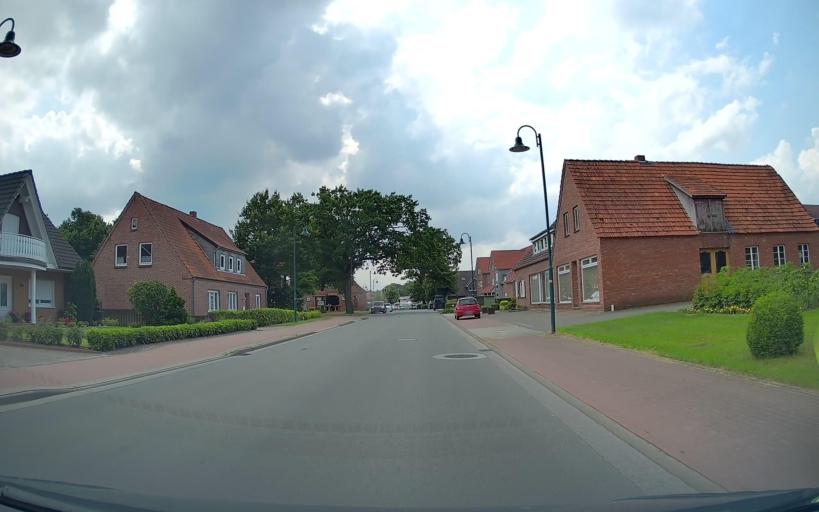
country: DE
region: Lower Saxony
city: Bosel
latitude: 53.0083
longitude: 7.9549
